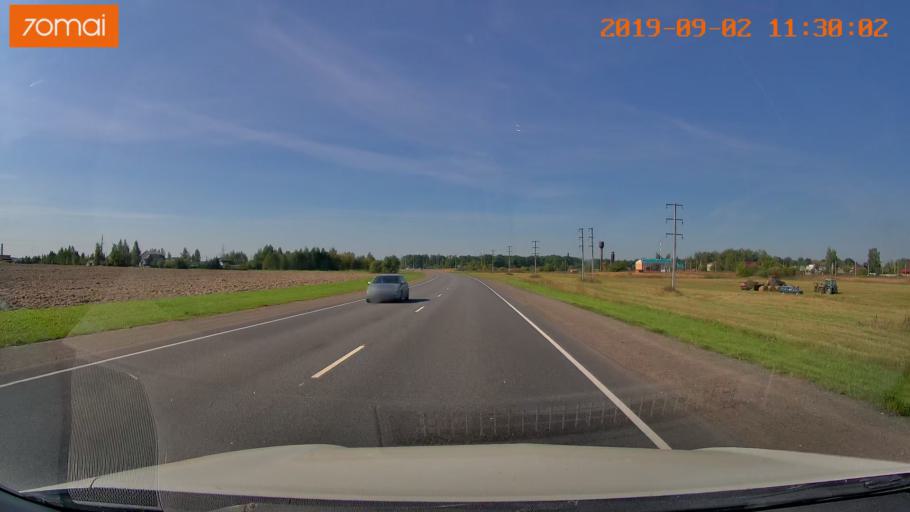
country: RU
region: Smolensk
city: Roslavl'
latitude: 53.9874
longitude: 32.8438
